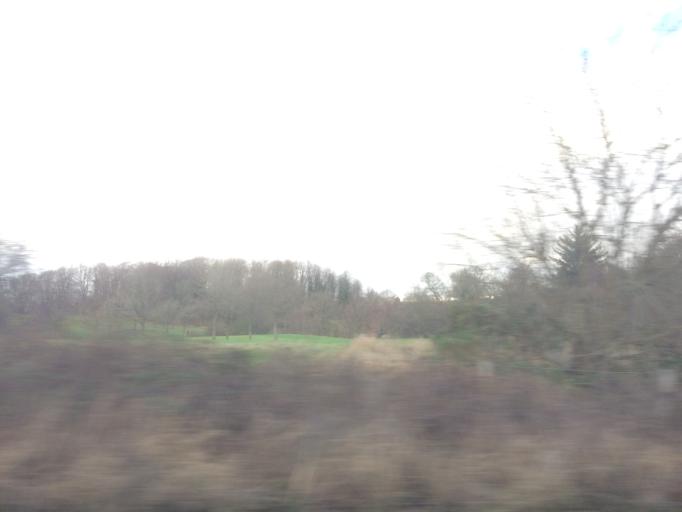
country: GB
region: Scotland
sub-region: East Renfrewshire
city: Newton Mearns
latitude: 55.7908
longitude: -4.3194
